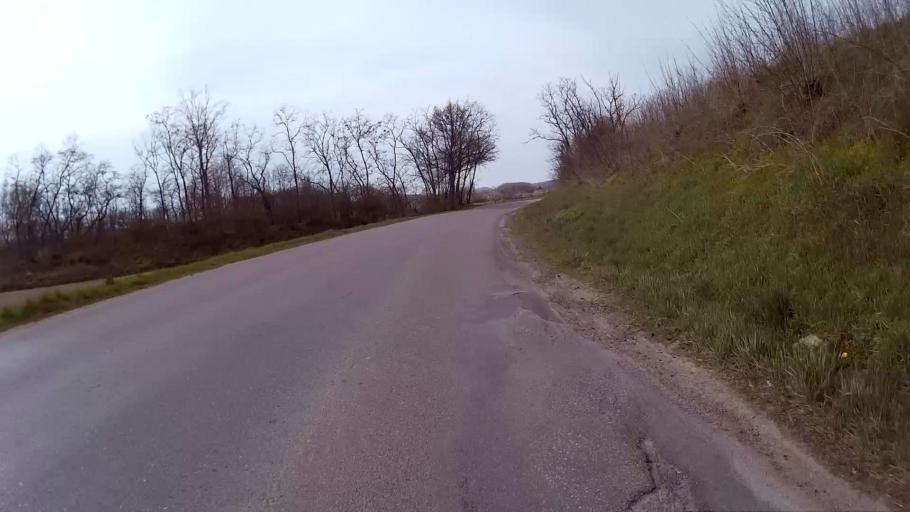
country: CZ
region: South Moravian
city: Dolni Kounice
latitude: 49.0503
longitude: 16.4926
